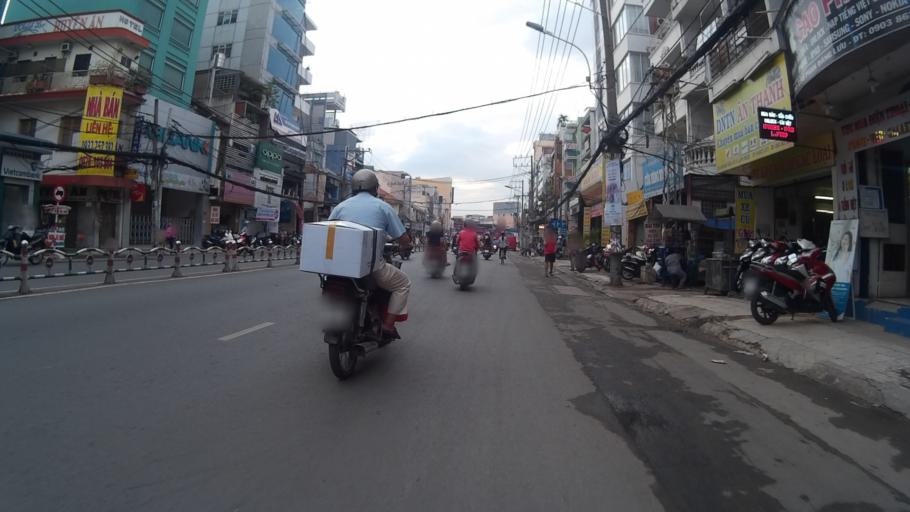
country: VN
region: Ho Chi Minh City
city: Quan Phu Nhuan
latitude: 10.8004
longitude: 106.6815
